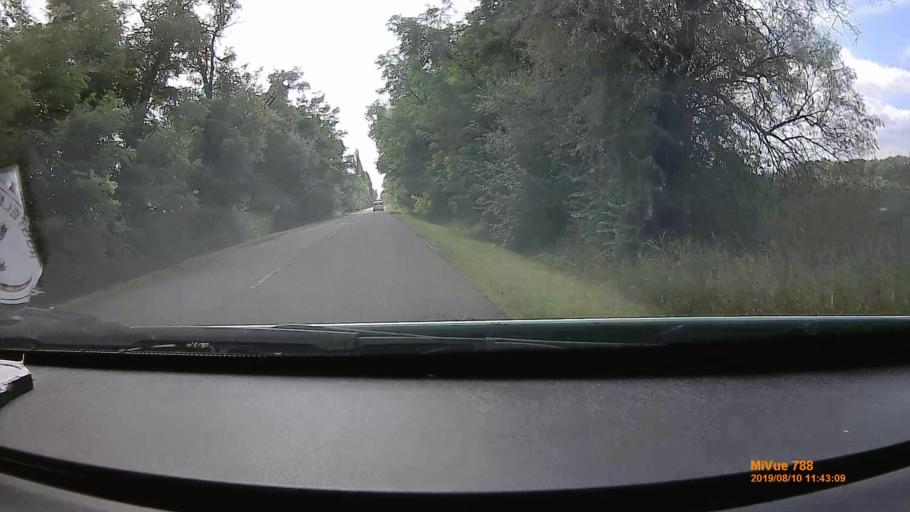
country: HU
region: Borsod-Abauj-Zemplen
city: Szentistvan
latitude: 47.7329
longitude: 20.6174
